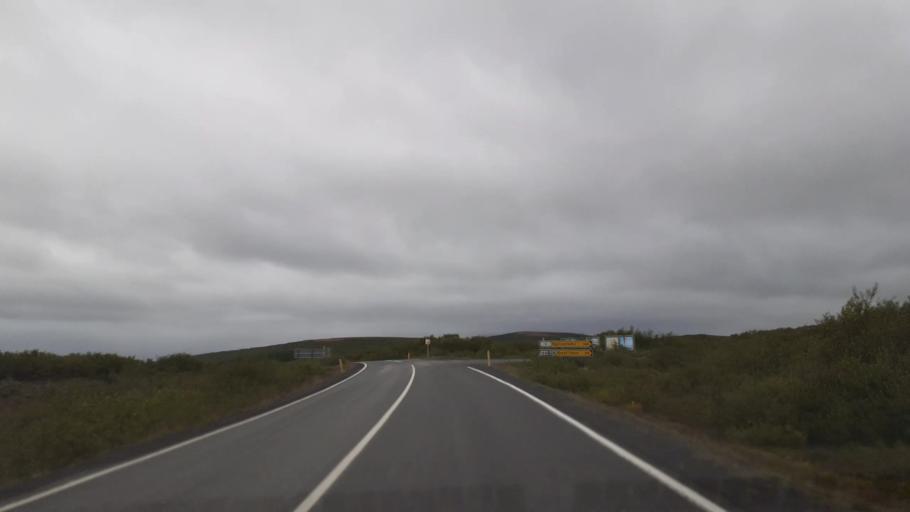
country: IS
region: Northeast
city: Husavik
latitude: 66.0355
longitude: -16.4390
